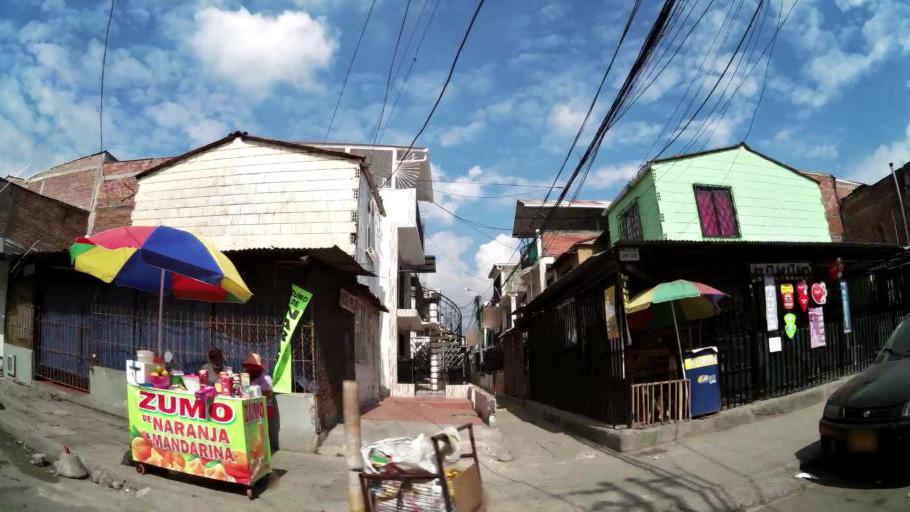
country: CO
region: Valle del Cauca
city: Cali
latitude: 3.4939
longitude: -76.4912
